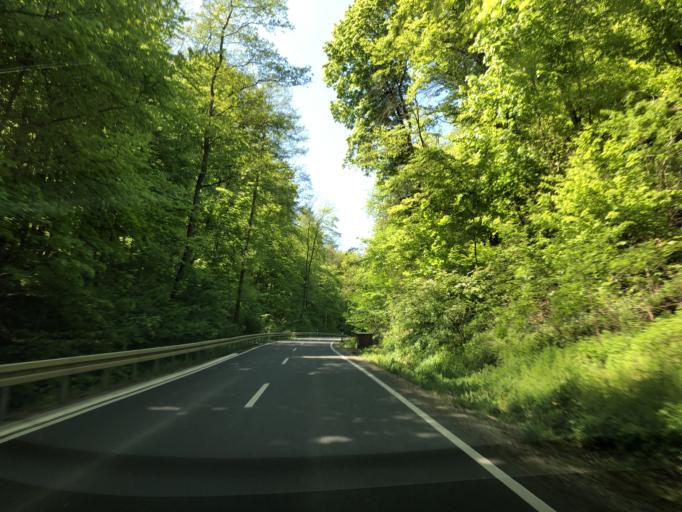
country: DE
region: Hesse
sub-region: Regierungsbezirk Kassel
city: Bad Sooden-Allendorf
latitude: 51.2692
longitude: 9.9508
